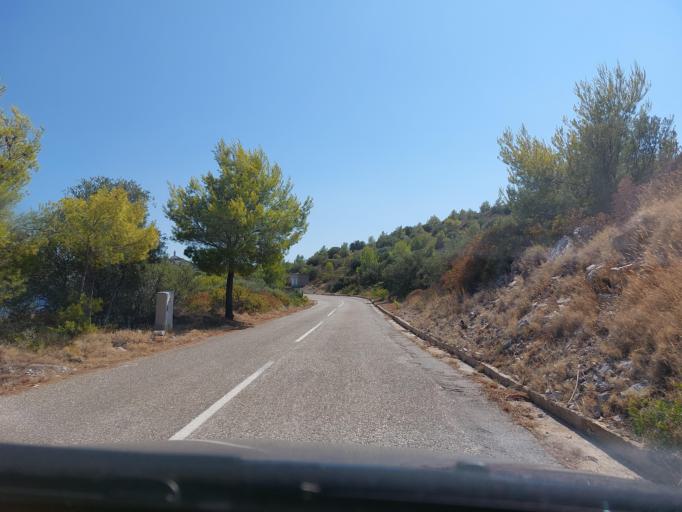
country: HR
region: Dubrovacko-Neretvanska
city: Smokvica
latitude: 42.7369
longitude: 16.8851
